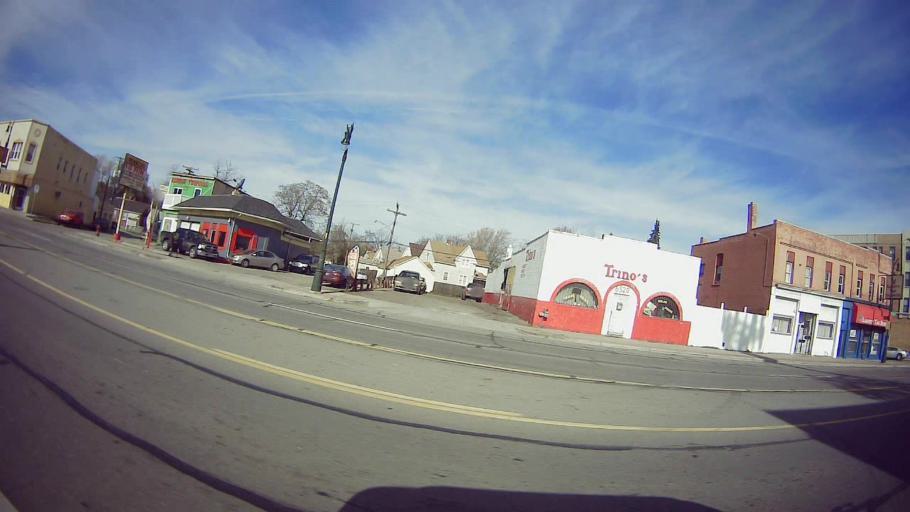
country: US
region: Michigan
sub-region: Wayne County
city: Dearborn
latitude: 42.3311
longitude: -83.1241
